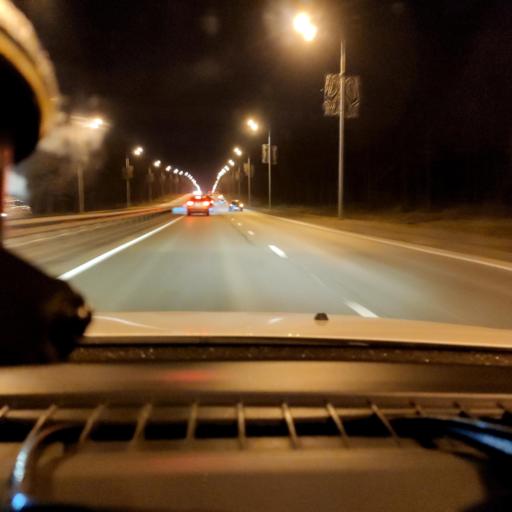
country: RU
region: Samara
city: Novosemeykino
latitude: 53.3257
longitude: 50.2309
